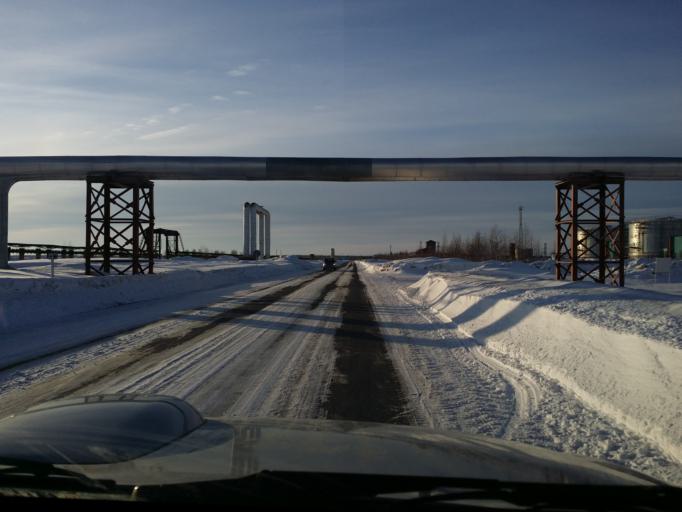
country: RU
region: Khanty-Mansiyskiy Avtonomnyy Okrug
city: Izluchinsk
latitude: 60.9758
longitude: 76.9321
